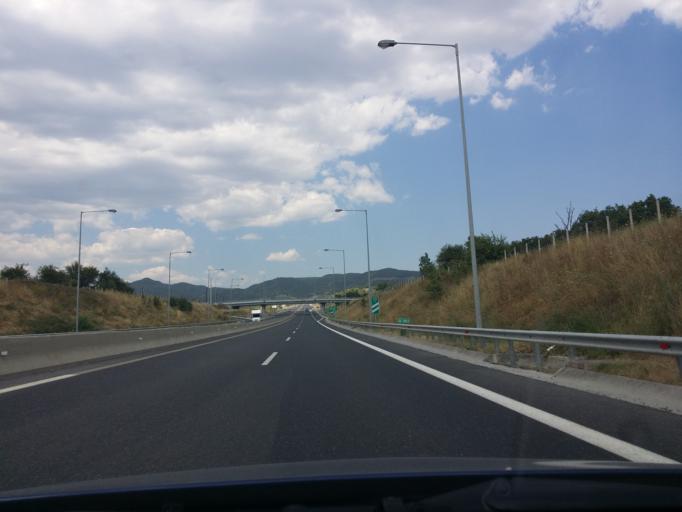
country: GR
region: Peloponnese
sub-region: Nomos Arkadias
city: Megalopoli
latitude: 37.3795
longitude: 22.1634
